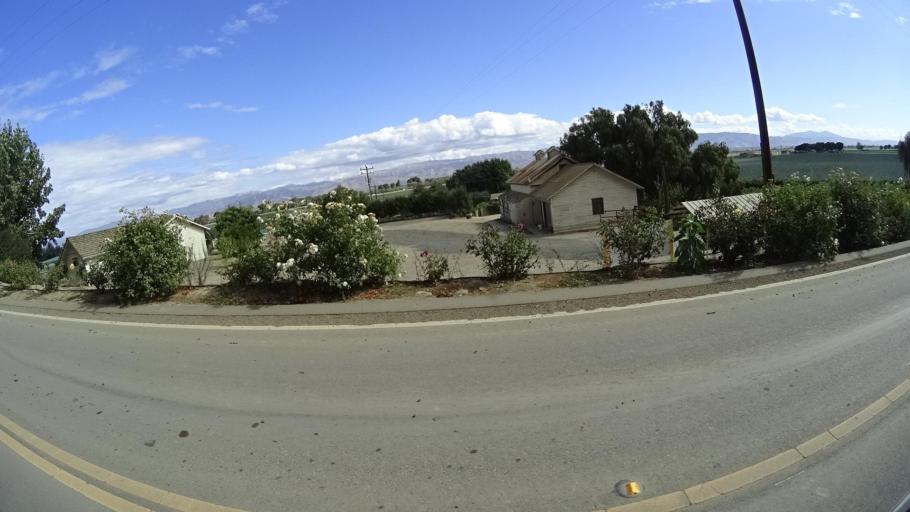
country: US
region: California
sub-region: Monterey County
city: Gonzales
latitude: 36.4796
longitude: -121.4855
